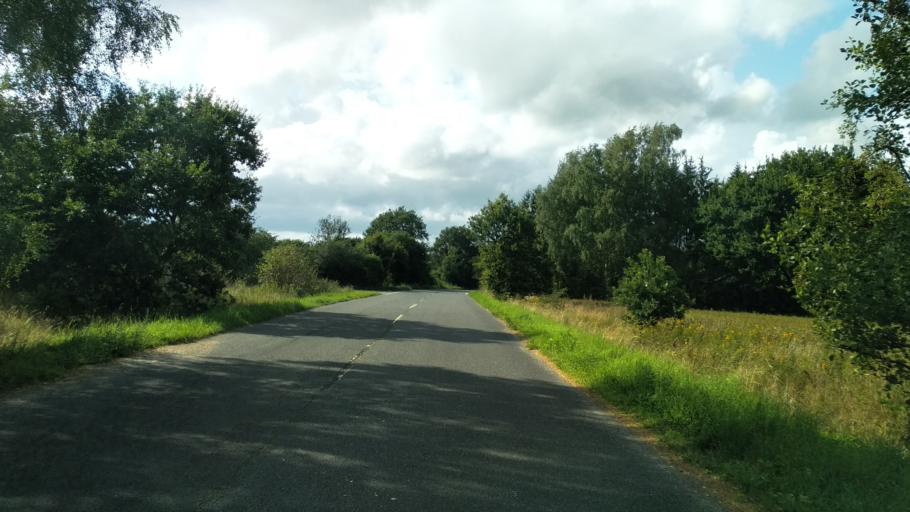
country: DE
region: Schleswig-Holstein
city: Neuberend
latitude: 54.5496
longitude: 9.5411
